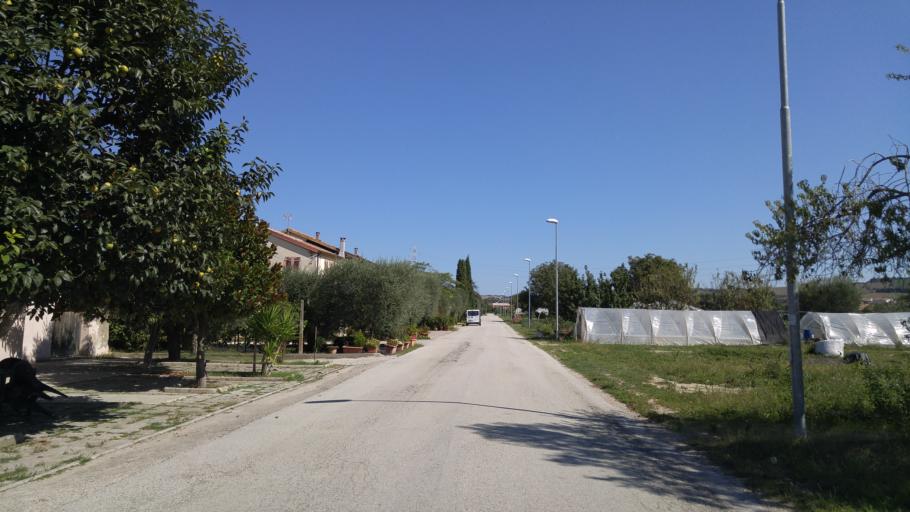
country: IT
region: The Marches
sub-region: Provincia di Pesaro e Urbino
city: Villanova
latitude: 43.7526
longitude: 12.9395
